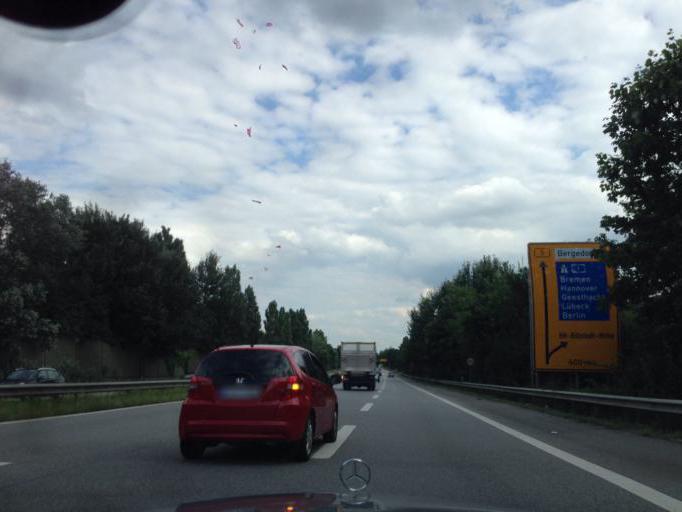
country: DE
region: Hamburg
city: Marienthal
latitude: 53.5432
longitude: 10.0875
